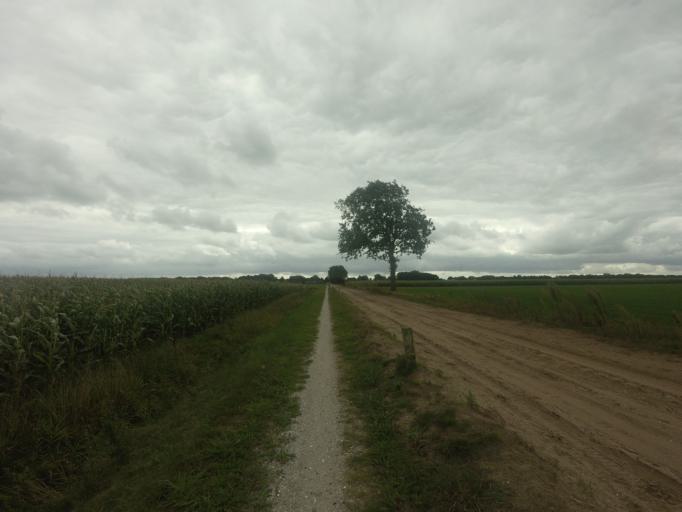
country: NL
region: Friesland
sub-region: Gemeente Weststellingwerf
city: Noordwolde
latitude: 52.9163
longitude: 6.1967
